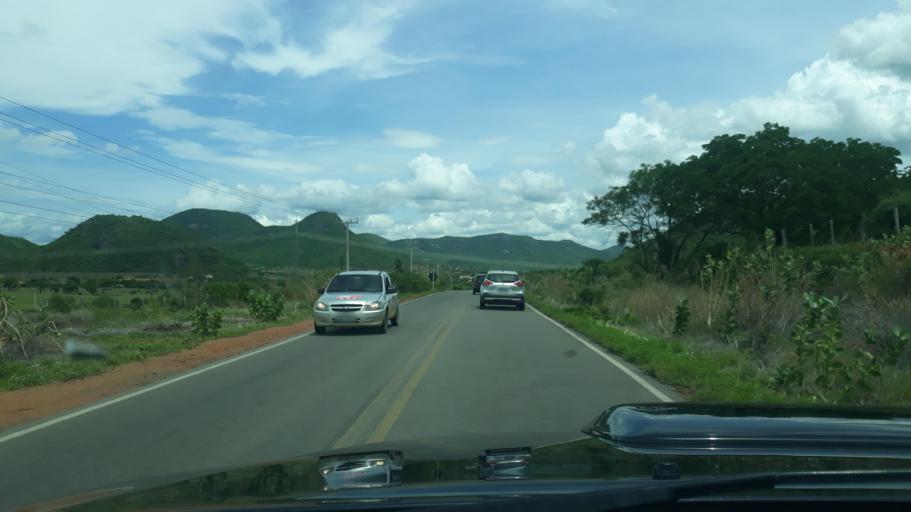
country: BR
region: Bahia
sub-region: Guanambi
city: Guanambi
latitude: -14.2606
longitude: -42.7239
